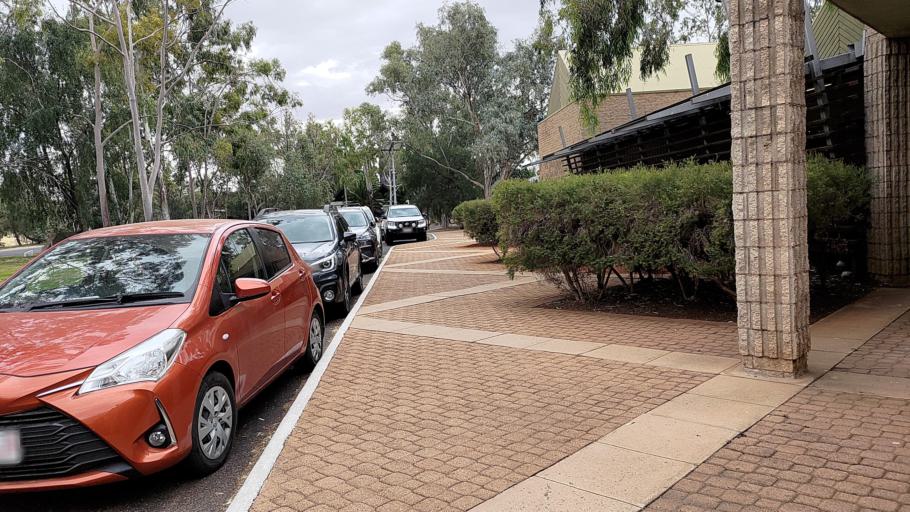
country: AU
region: Northern Territory
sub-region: Alice Springs
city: Alice Springs
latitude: -23.7150
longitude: 133.8793
